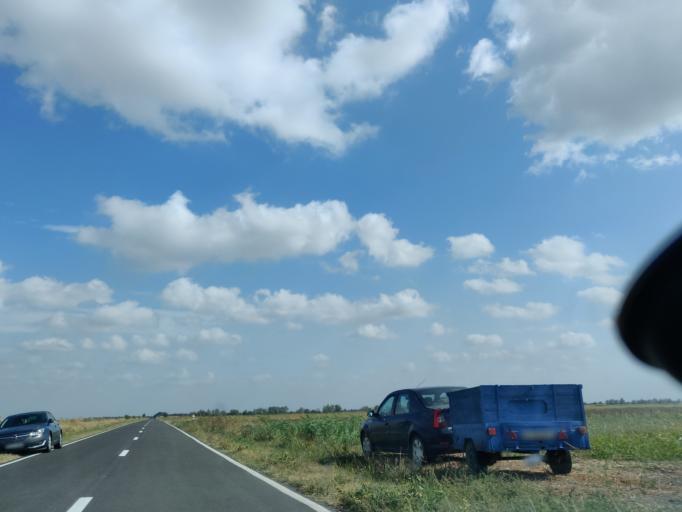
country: RO
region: Vrancea
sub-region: Comuna Maicanesti
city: Ramniceni
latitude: 45.4662
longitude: 27.4210
